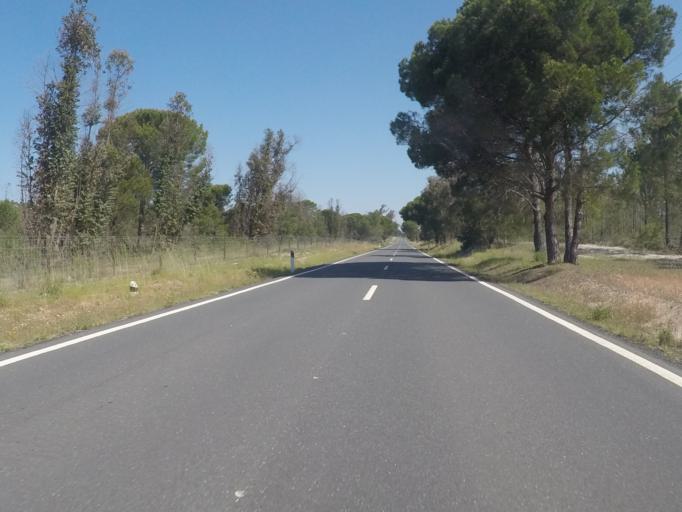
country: PT
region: Setubal
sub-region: Santiago do Cacem
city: Santo Andre
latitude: 38.2301
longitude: -8.7353
